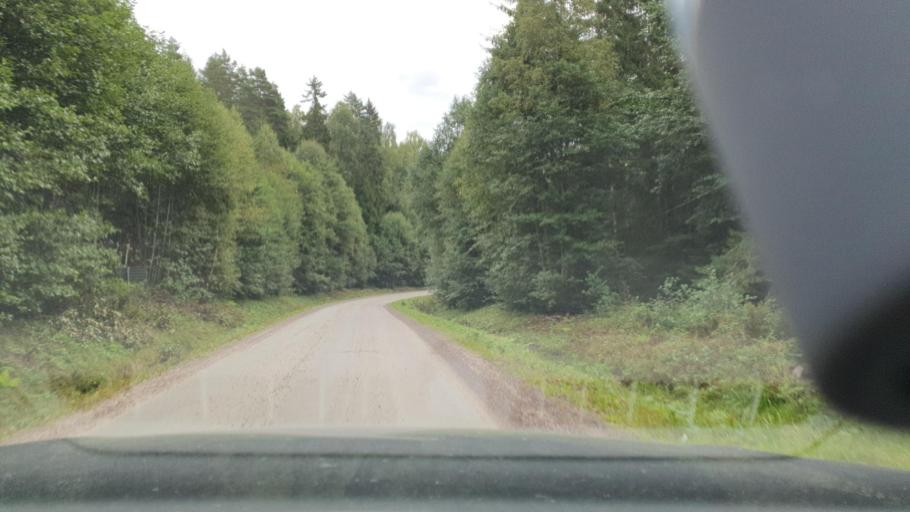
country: SE
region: Vaermland
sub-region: Munkfors Kommun
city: Munkfors
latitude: 59.9844
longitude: 13.4046
